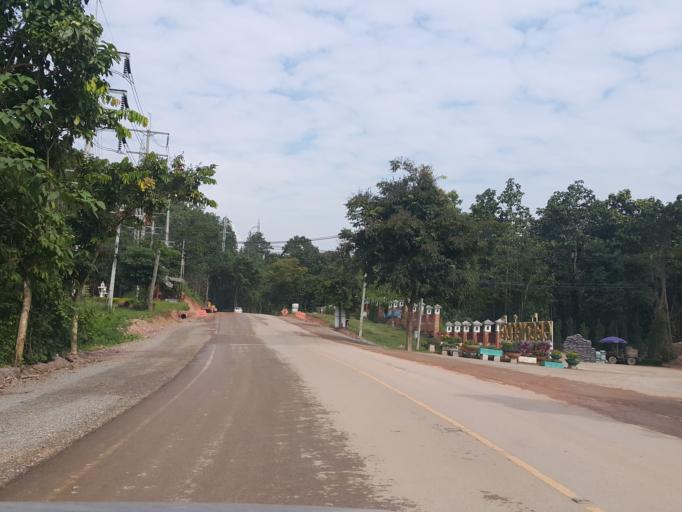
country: TH
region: Mae Hong Son
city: Mae Hong Son
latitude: 19.3348
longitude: 97.9660
